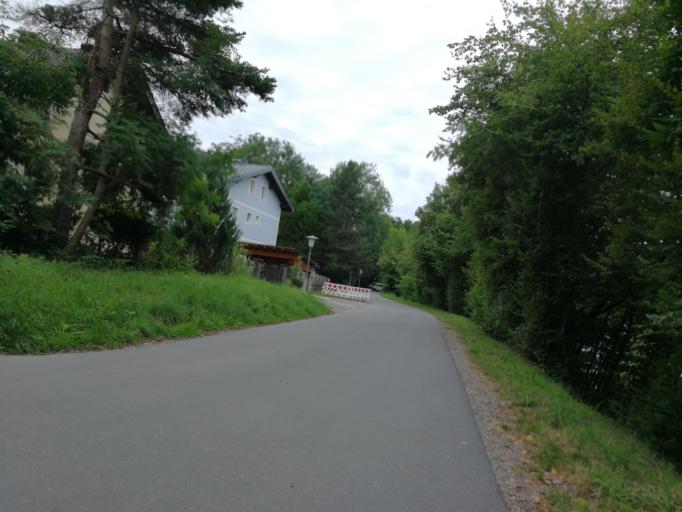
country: DE
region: Bavaria
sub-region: Upper Bavaria
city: Ainring
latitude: 47.7940
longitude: 12.9565
